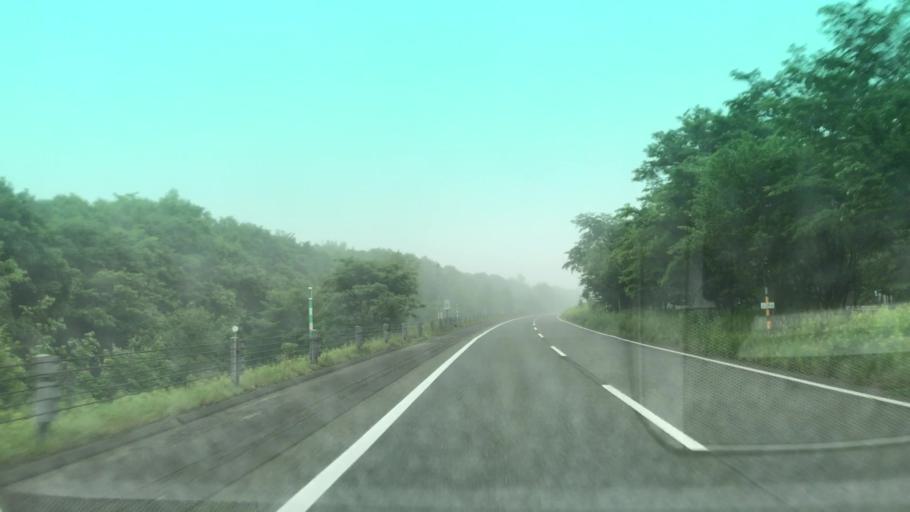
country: JP
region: Hokkaido
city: Chitose
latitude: 42.7985
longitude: 141.6264
